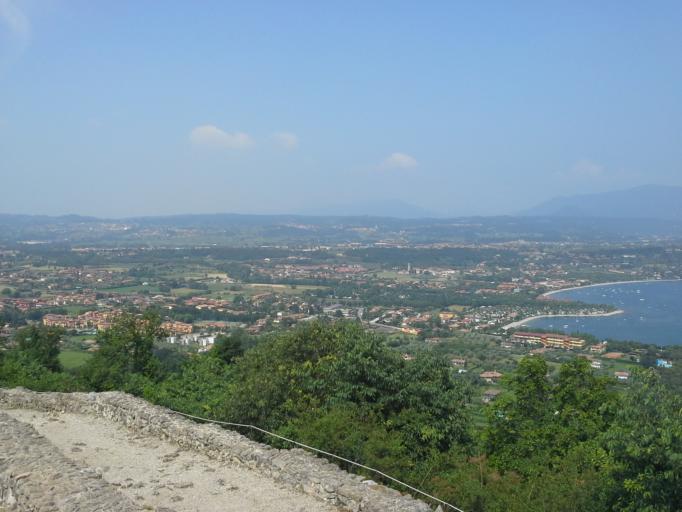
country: IT
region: Lombardy
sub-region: Provincia di Brescia
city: Solarolo
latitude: 45.5576
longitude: 10.5722
